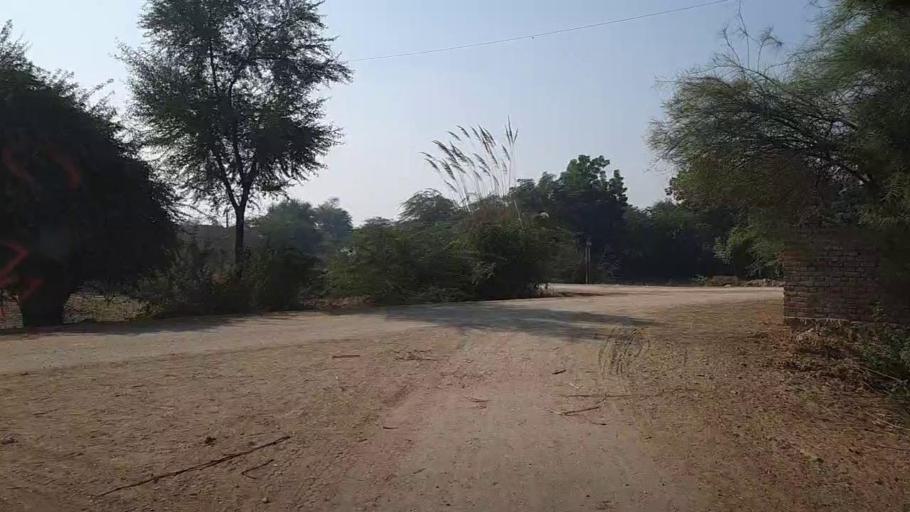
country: PK
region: Sindh
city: Bozdar
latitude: 27.2441
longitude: 68.6044
